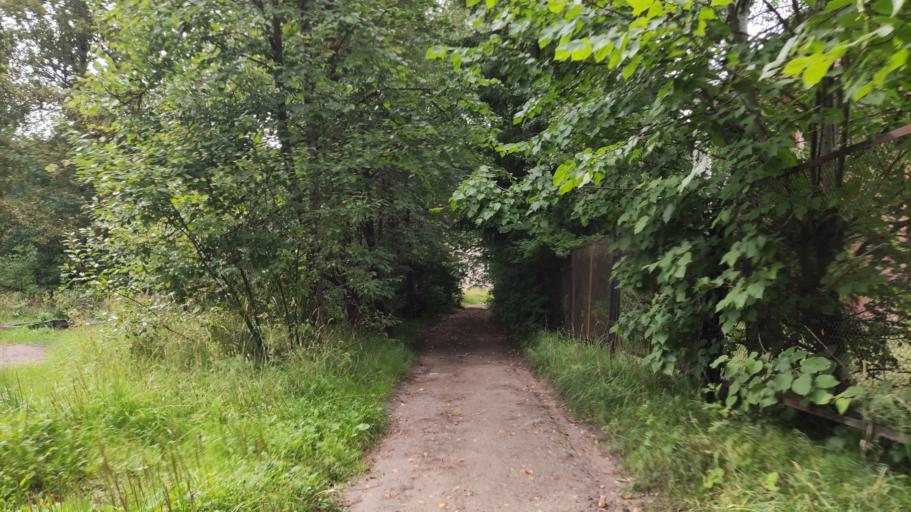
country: RU
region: Tverskaya
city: Rzhev
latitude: 56.2410
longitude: 34.3290
